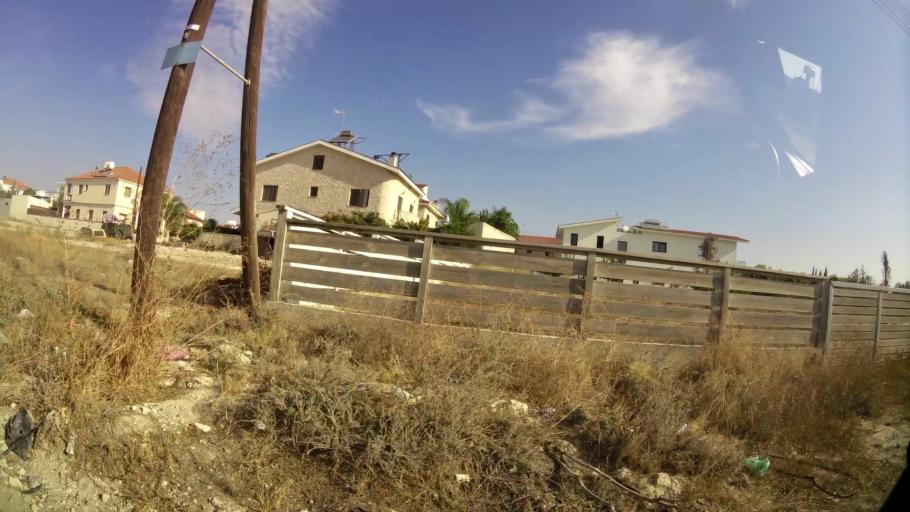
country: CY
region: Larnaka
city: Aradippou
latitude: 34.9525
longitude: 33.5988
